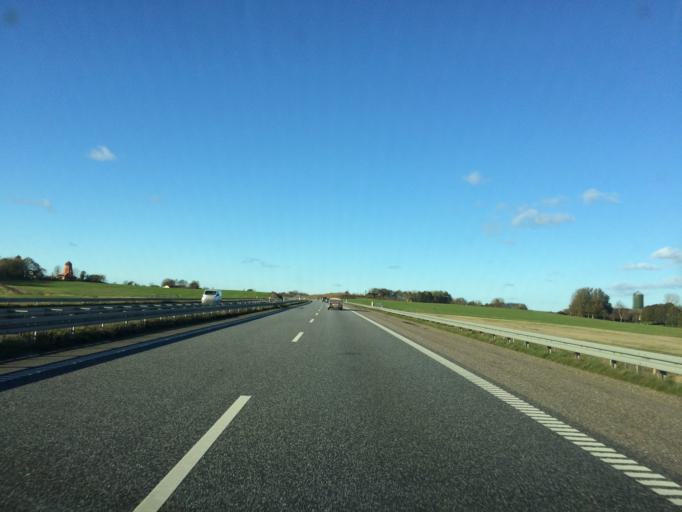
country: DK
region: Central Jutland
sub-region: Hedensted Kommune
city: Torring
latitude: 55.8111
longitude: 9.5561
